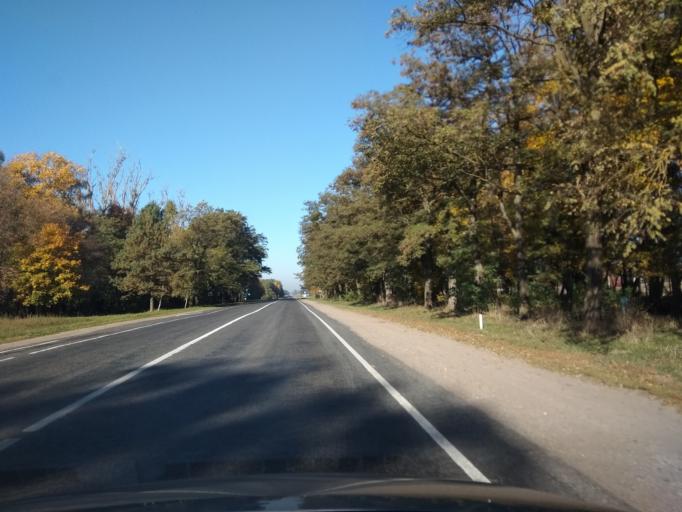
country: BY
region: Brest
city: Malaryta
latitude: 51.9323
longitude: 24.0564
